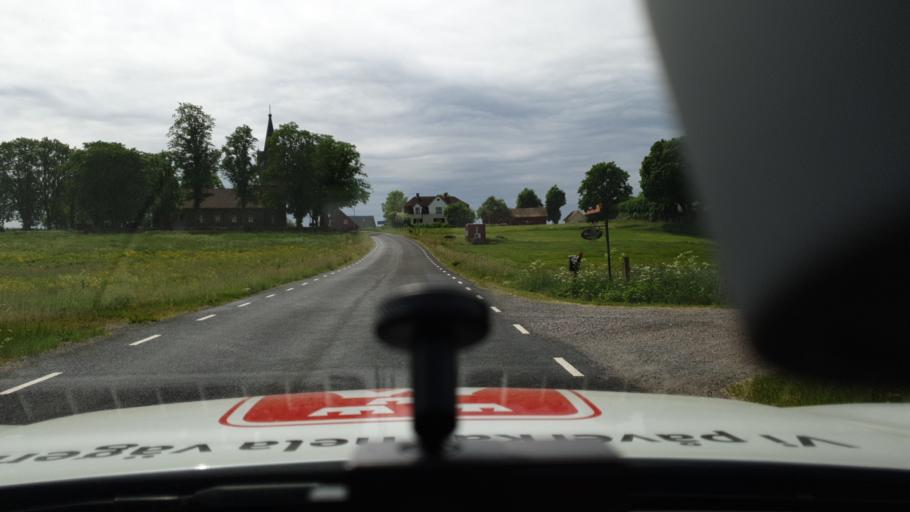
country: SE
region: Joenkoeping
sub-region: Mullsjo Kommun
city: Mullsjoe
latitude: 58.0149
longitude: 13.6930
